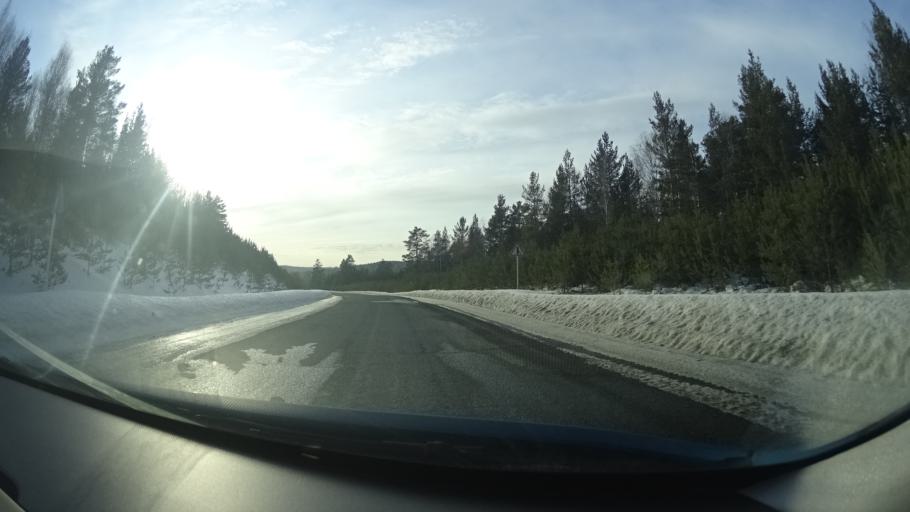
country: RU
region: Bashkortostan
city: Lomovka
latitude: 53.6720
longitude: 58.2332
